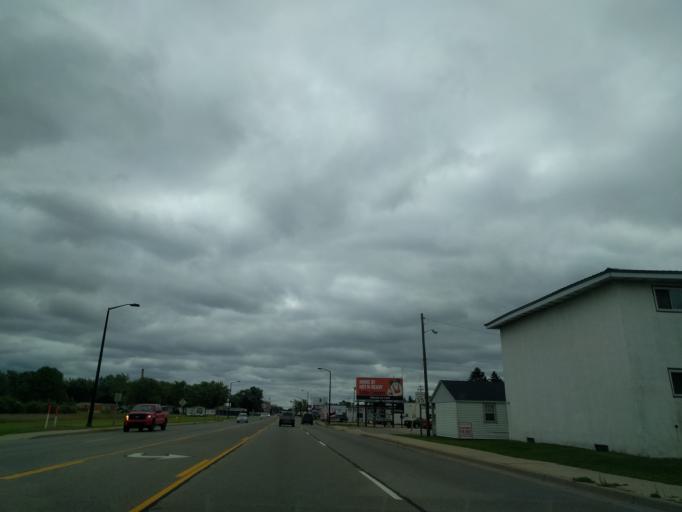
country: US
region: Michigan
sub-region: Menominee County
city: Menominee
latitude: 45.1321
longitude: -87.6127
